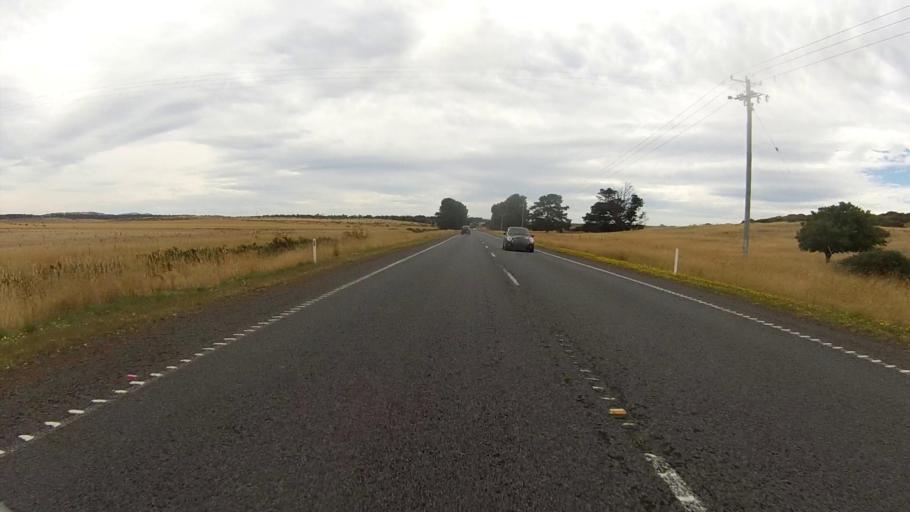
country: AU
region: Tasmania
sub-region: Northern Midlands
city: Evandale
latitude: -41.8519
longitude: 147.4516
